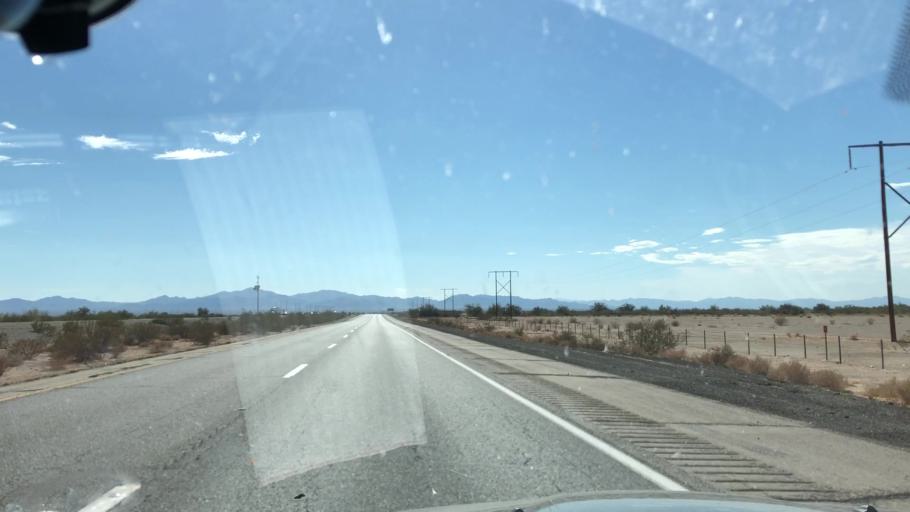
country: US
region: California
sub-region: Riverside County
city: Mesa Verde
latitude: 33.6063
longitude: -114.9679
